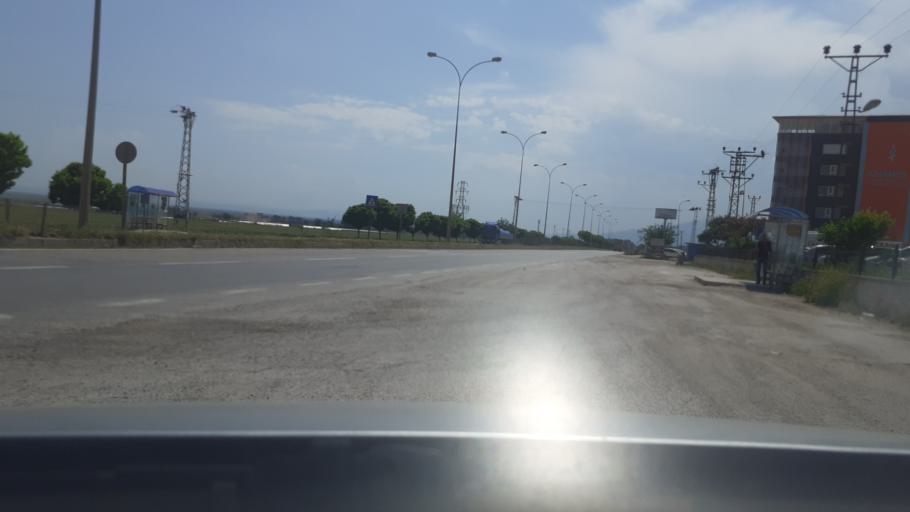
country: TR
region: Hatay
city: Kirikhan
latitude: 36.4798
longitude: 36.3560
